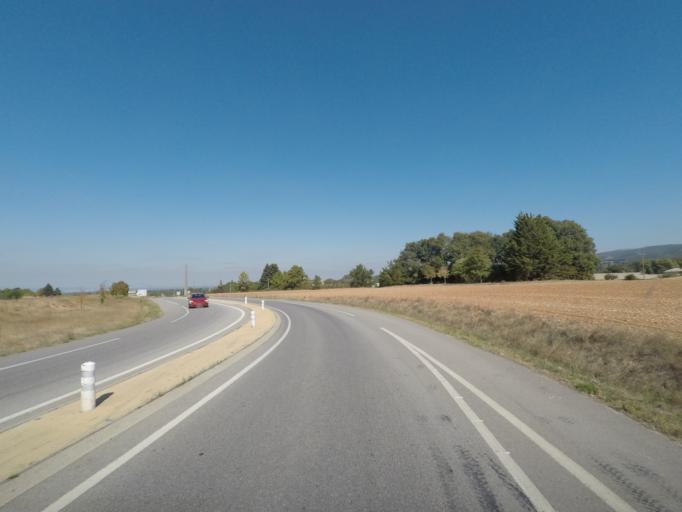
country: FR
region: Rhone-Alpes
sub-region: Departement de la Drome
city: Upie
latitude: 44.8198
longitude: 5.0110
